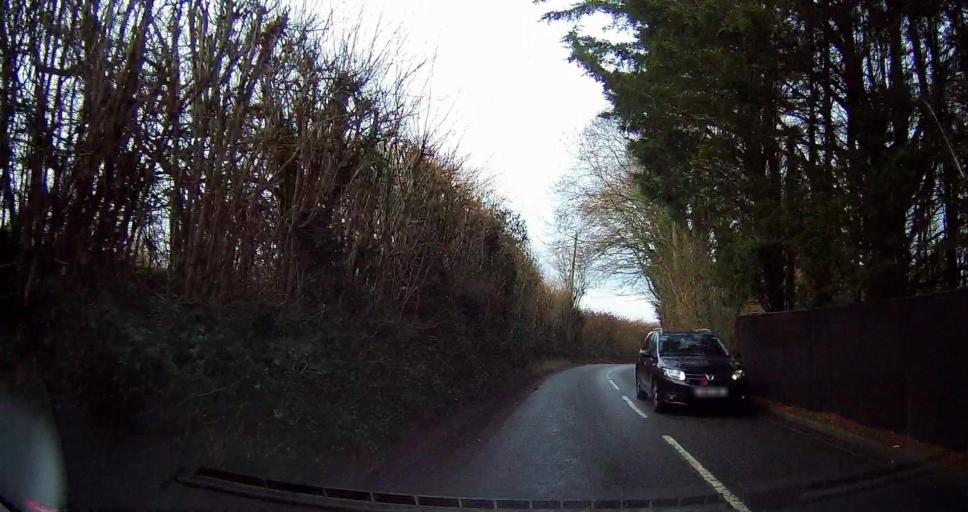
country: GB
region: England
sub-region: Greater London
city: Orpington
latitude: 51.3394
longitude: 0.0803
